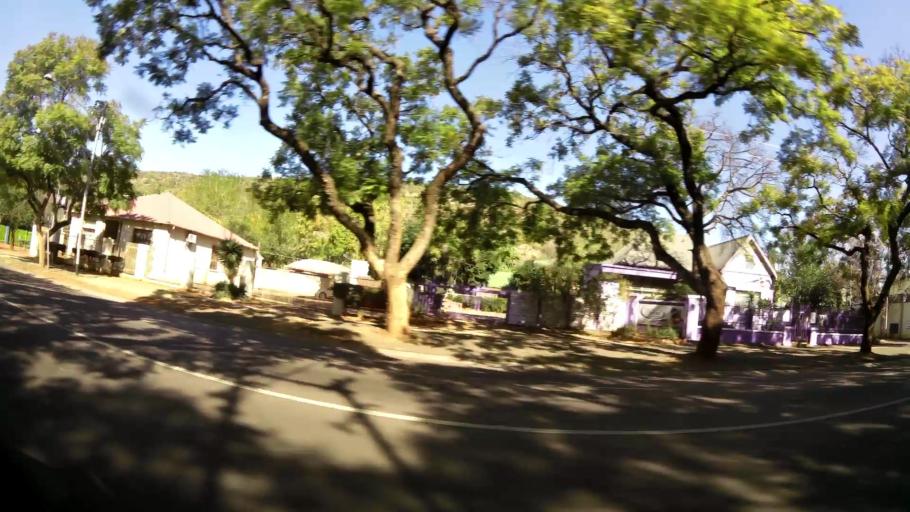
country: ZA
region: Gauteng
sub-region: City of Tshwane Metropolitan Municipality
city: Pretoria
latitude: -25.7344
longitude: 28.2104
